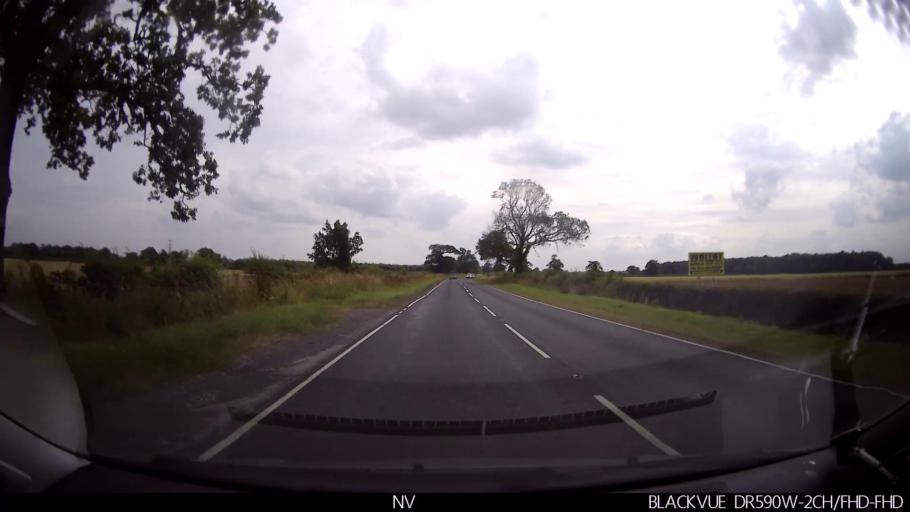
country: GB
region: England
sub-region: North Yorkshire
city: Marishes
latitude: 54.1656
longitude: -0.7658
